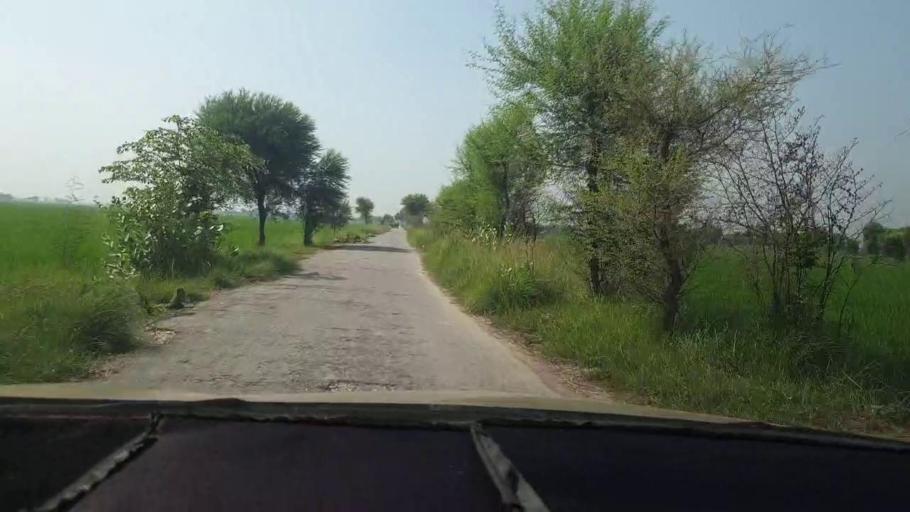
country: PK
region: Sindh
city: Kambar
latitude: 27.5795
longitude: 68.0554
